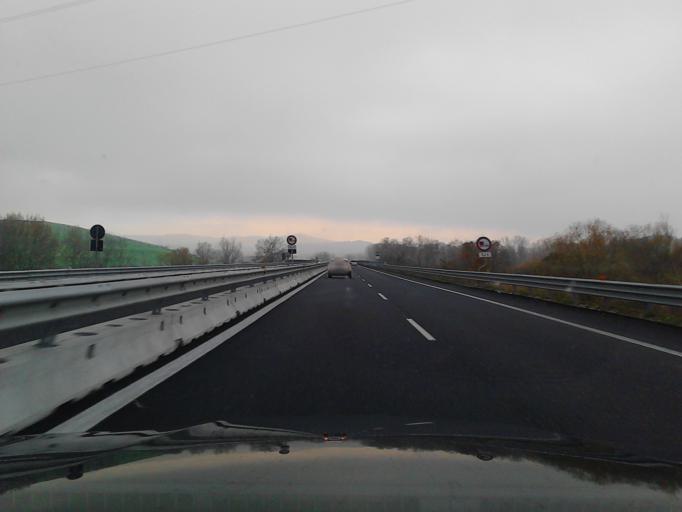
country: IT
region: Abruzzo
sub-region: Provincia di Pescara
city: Fonte Umano-San Martino Alta
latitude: 42.5000
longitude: 14.1163
